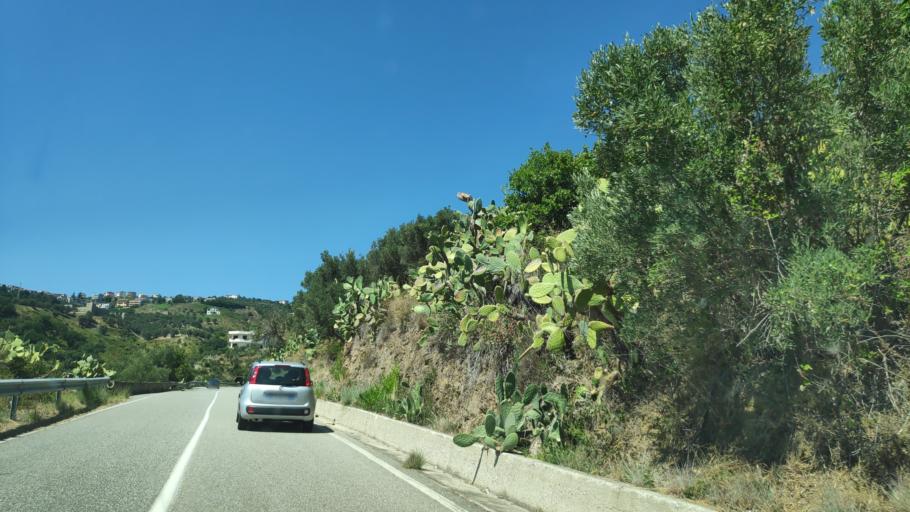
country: IT
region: Calabria
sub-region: Provincia di Catanzaro
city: Montauro
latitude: 38.7461
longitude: 16.5200
